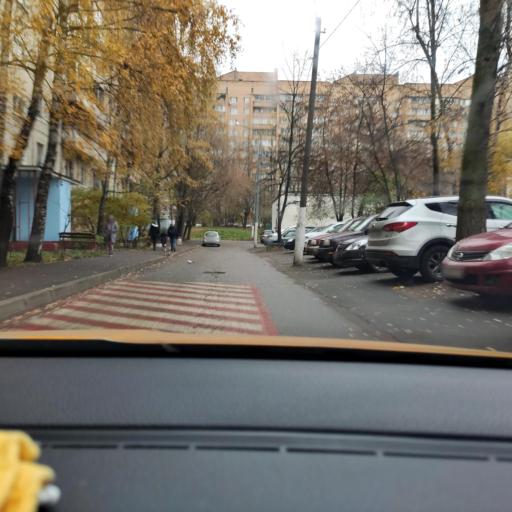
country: RU
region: Moscow
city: Otradnoye
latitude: 55.8714
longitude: 37.6009
